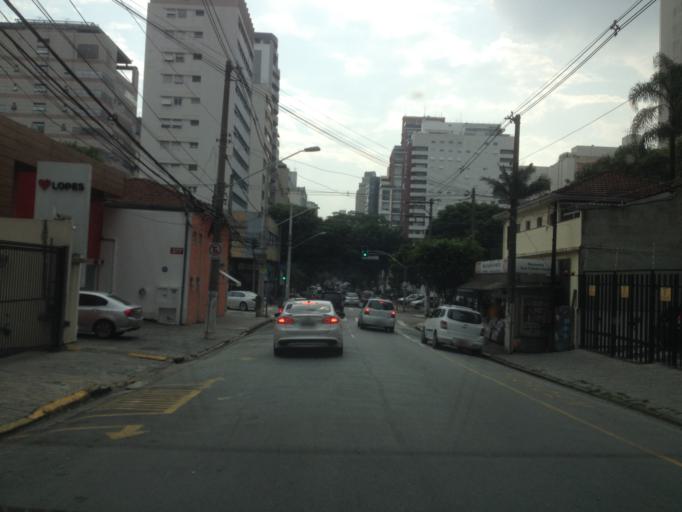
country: BR
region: Sao Paulo
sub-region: Sao Paulo
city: Sao Paulo
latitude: -23.5818
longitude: -46.6738
